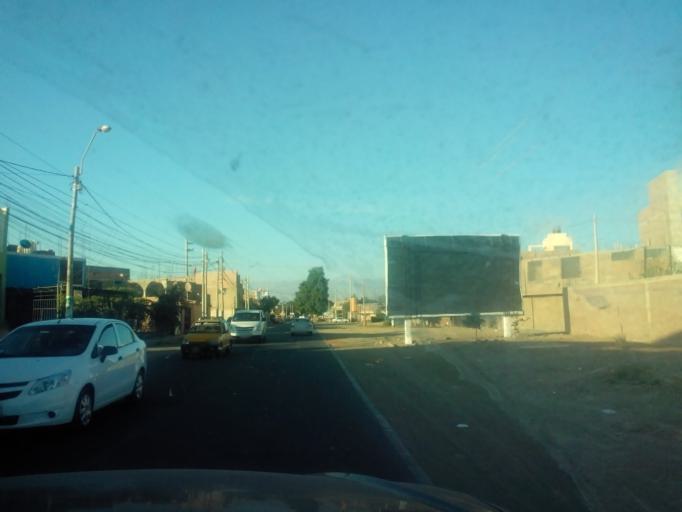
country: PE
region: Ica
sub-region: Provincia de Ica
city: Ica
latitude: -14.0798
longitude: -75.7475
